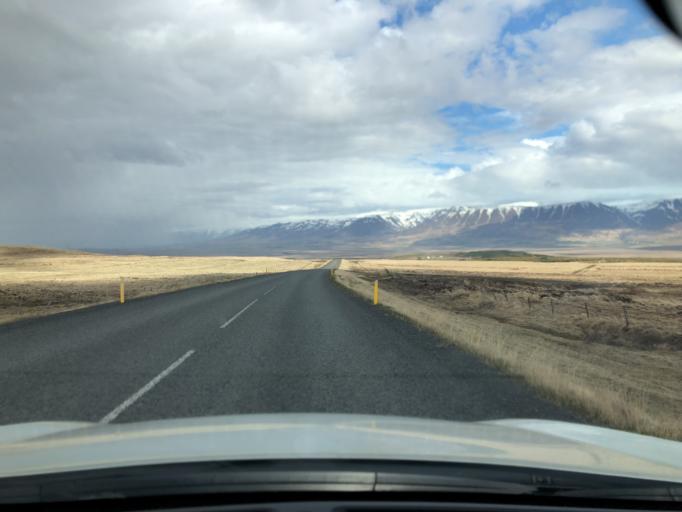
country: IS
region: Northwest
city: Saudarkrokur
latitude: 65.5362
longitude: -19.5096
